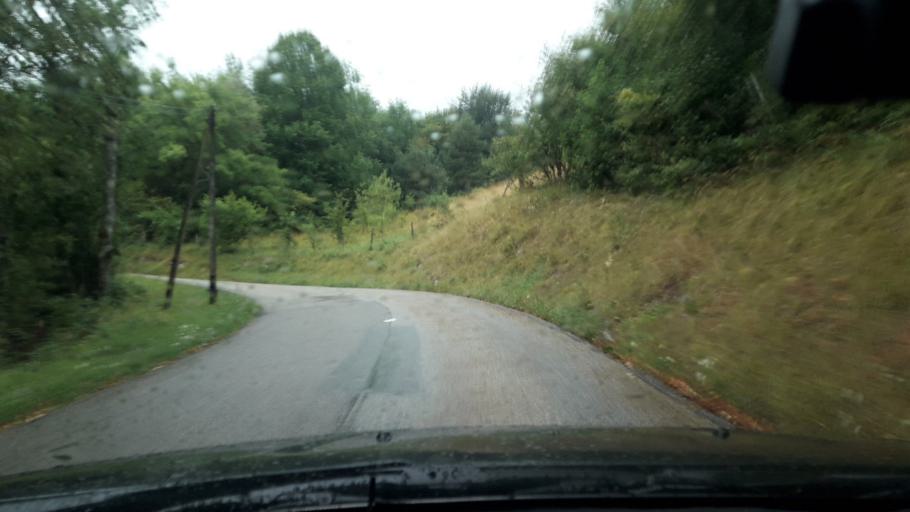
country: FR
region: Rhone-Alpes
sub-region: Departement de la Savoie
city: Saint-Baldoph
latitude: 45.5157
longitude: 5.9330
